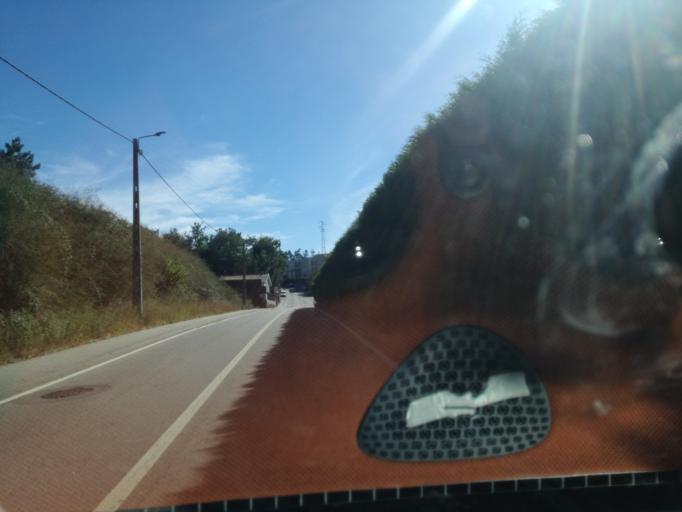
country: PT
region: Braga
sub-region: Guimaraes
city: Guimaraes
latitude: 41.4595
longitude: -8.2934
